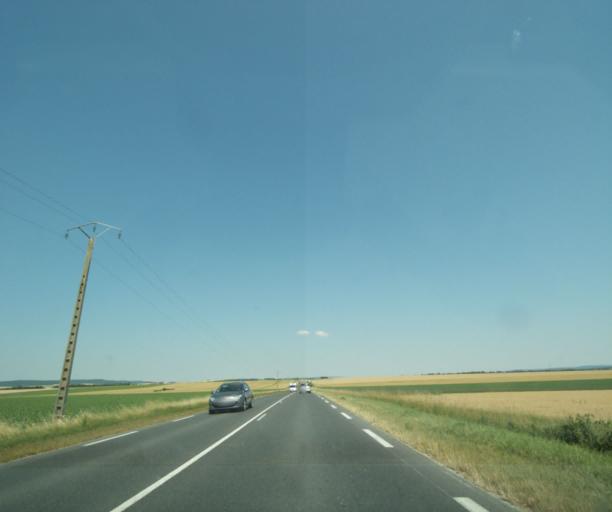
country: FR
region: Champagne-Ardenne
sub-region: Departement de la Marne
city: Mourmelon-le-Grand
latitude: 49.0907
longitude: 4.2737
